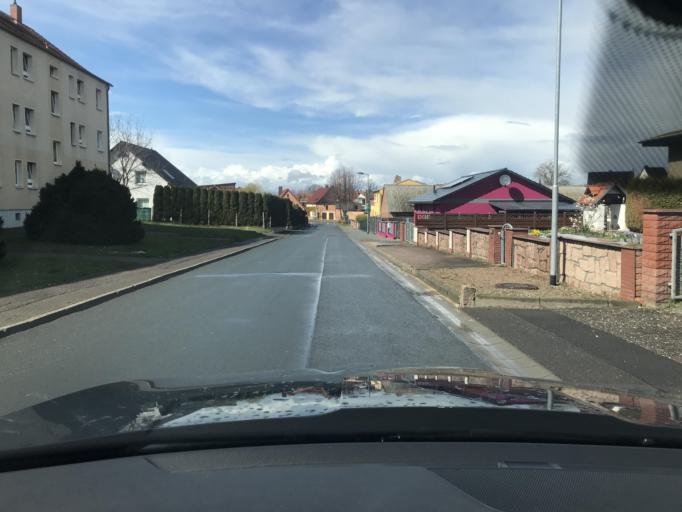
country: DE
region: Saxony-Anhalt
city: Hoym
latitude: 51.7307
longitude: 11.3535
